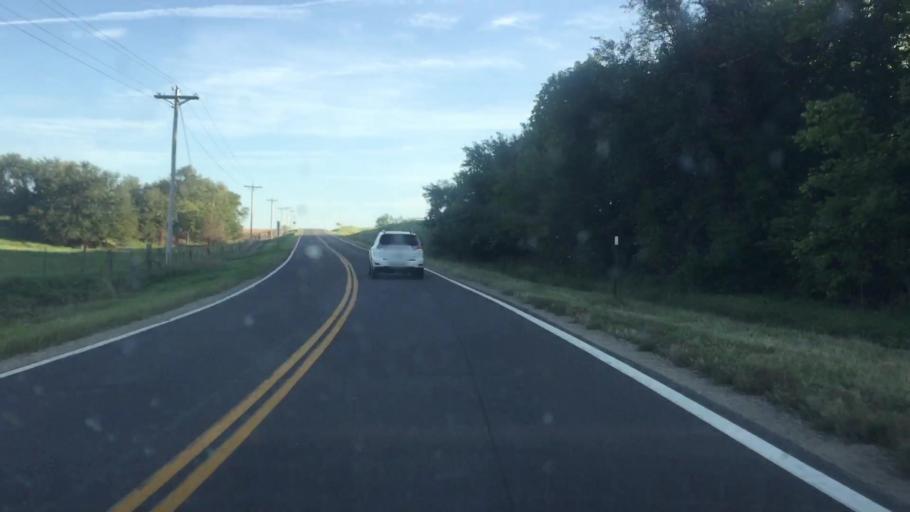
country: US
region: Kansas
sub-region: Brown County
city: Horton
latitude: 39.5696
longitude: -95.5268
